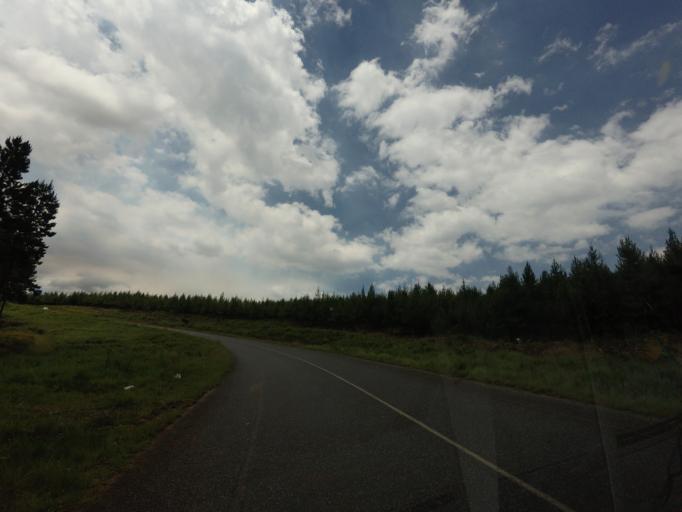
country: ZA
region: Mpumalanga
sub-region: Ehlanzeni District
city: Graksop
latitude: -24.9643
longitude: 30.8130
